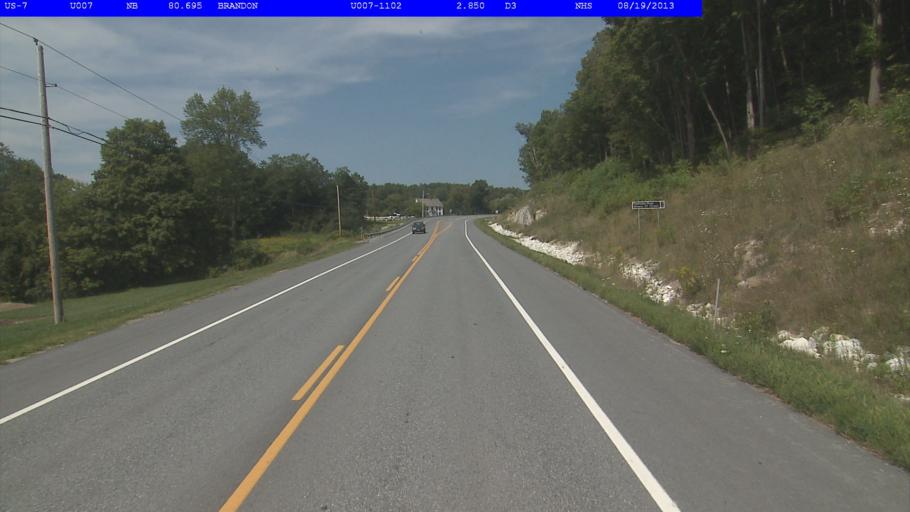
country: US
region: Vermont
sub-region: Rutland County
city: Brandon
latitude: 43.7877
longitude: -73.0736
